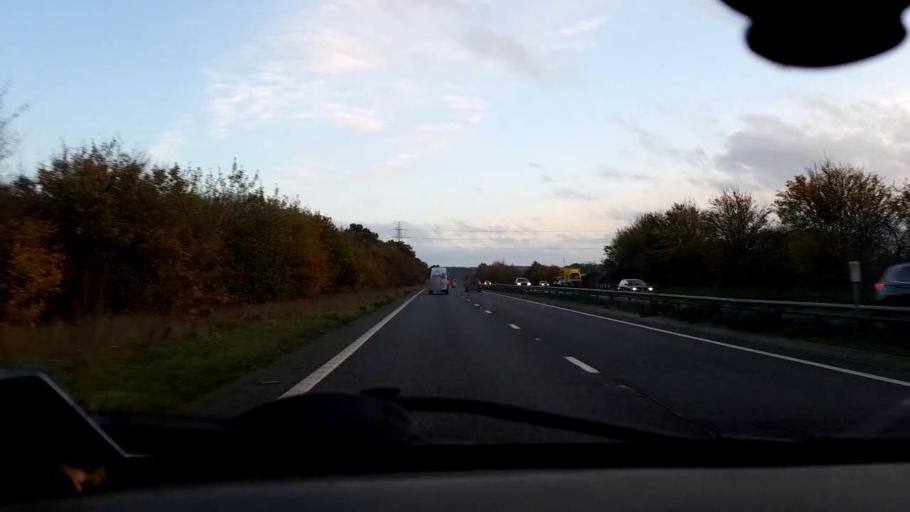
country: GB
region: England
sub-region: Norfolk
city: Costessey
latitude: 52.6442
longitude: 1.1911
